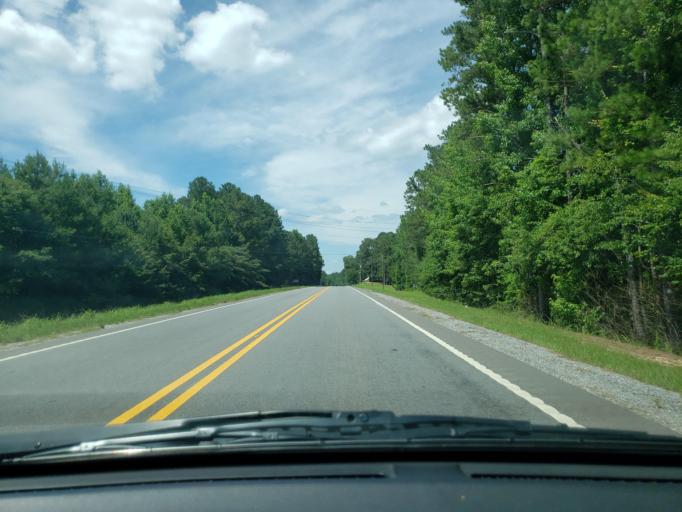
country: US
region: Alabama
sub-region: Elmore County
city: Eclectic
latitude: 32.6569
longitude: -85.9439
